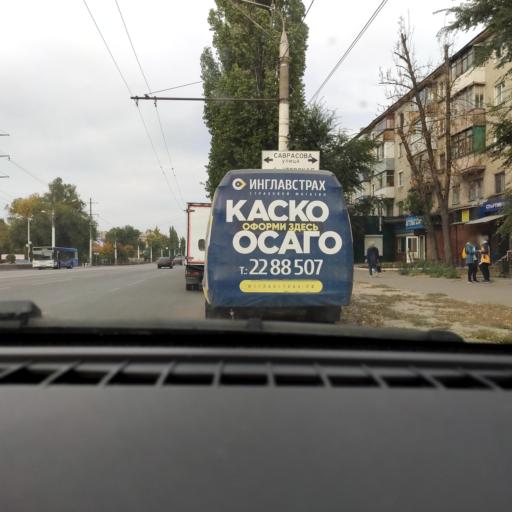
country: RU
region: Voronezj
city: Maslovka
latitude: 51.6054
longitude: 39.2372
